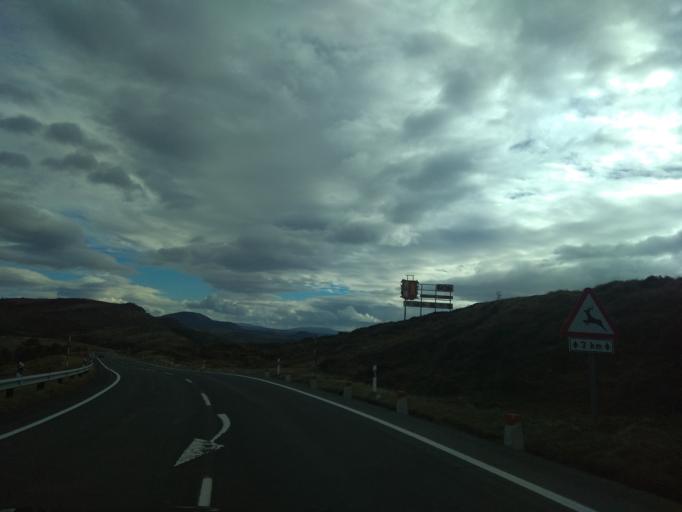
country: ES
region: Castille and Leon
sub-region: Provincia de Burgos
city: Arija
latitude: 43.0408
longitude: -3.8769
